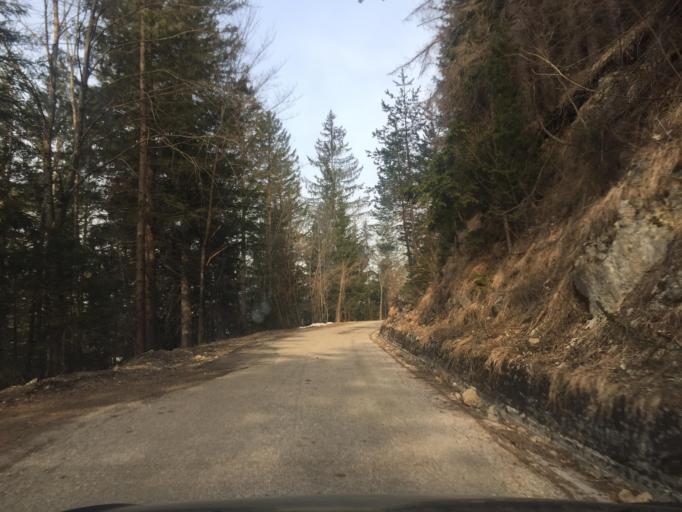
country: IT
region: Friuli Venezia Giulia
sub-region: Provincia di Udine
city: Tarvisio
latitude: 46.4973
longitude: 13.6388
